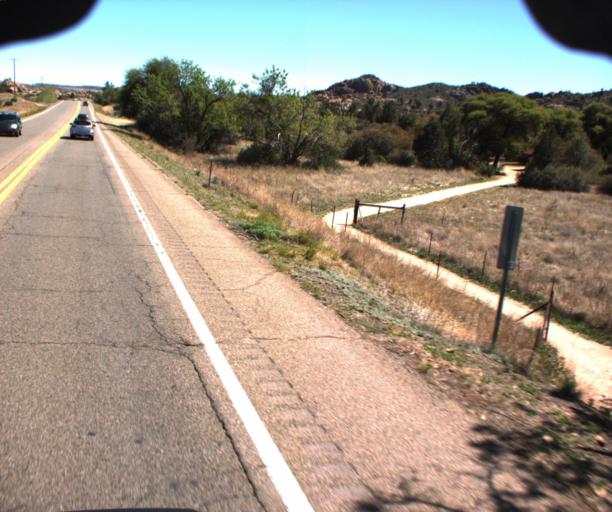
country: US
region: Arizona
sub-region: Yavapai County
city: Prescott
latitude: 34.6222
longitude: -112.4258
